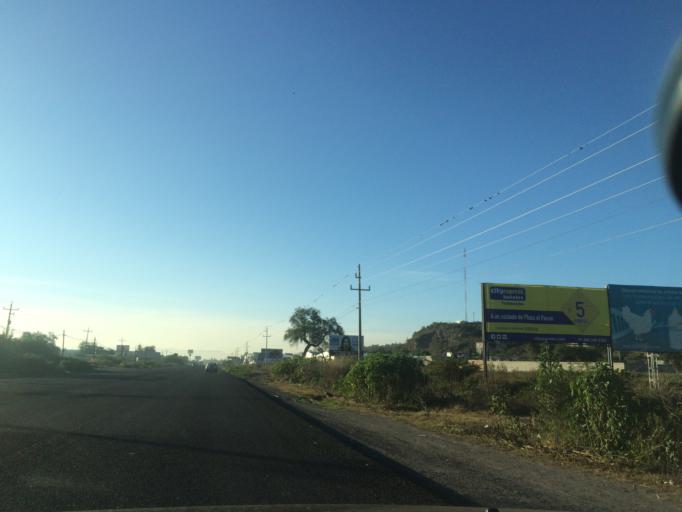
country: MX
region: Puebla
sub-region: Santiago Miahuatlan
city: San Jose Monte Chiquito
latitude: 18.4832
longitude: -97.4494
